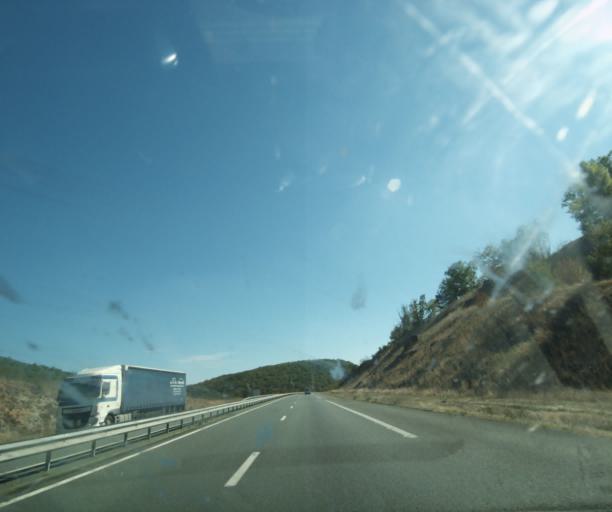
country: FR
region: Midi-Pyrenees
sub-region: Departement du Lot
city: Souillac
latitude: 44.8406
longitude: 1.4928
